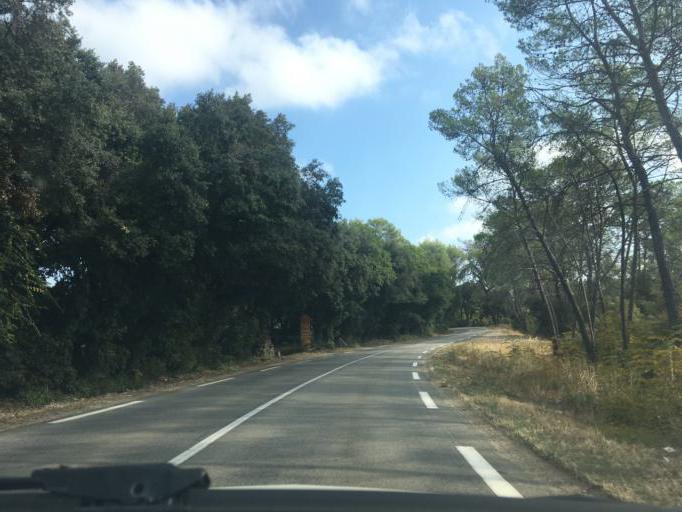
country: FR
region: Provence-Alpes-Cote d'Azur
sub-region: Departement du Var
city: Flayosc
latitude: 43.5070
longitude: 6.4217
